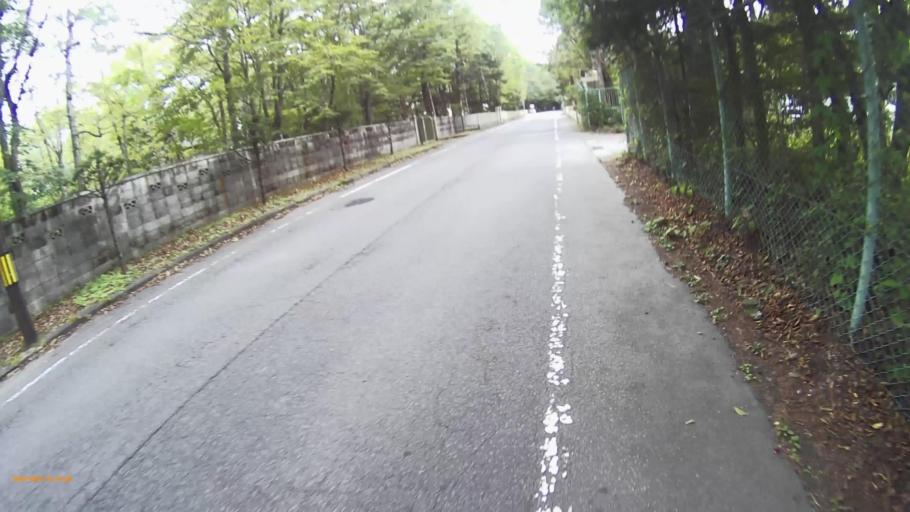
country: JP
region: Shizuoka
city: Gotemba
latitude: 35.4138
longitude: 138.8578
